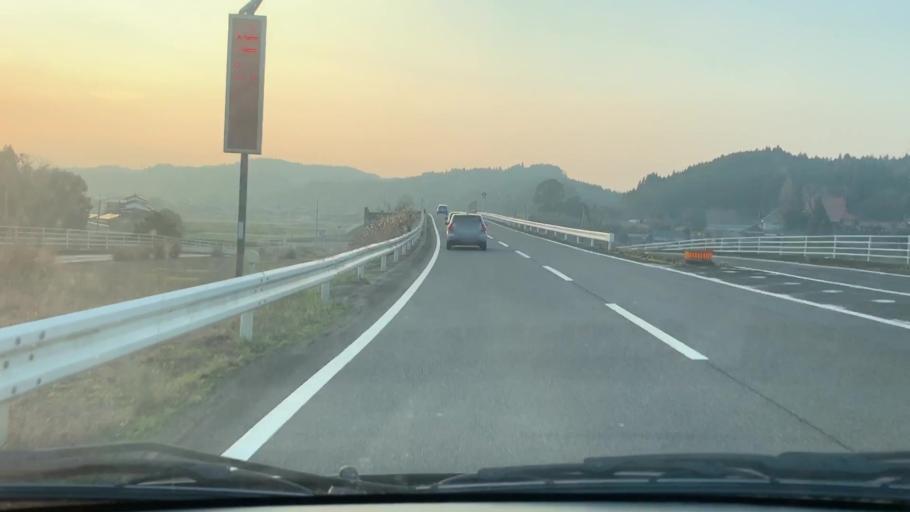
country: JP
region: Saga Prefecture
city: Imaricho-ko
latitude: 33.2640
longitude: 129.9643
